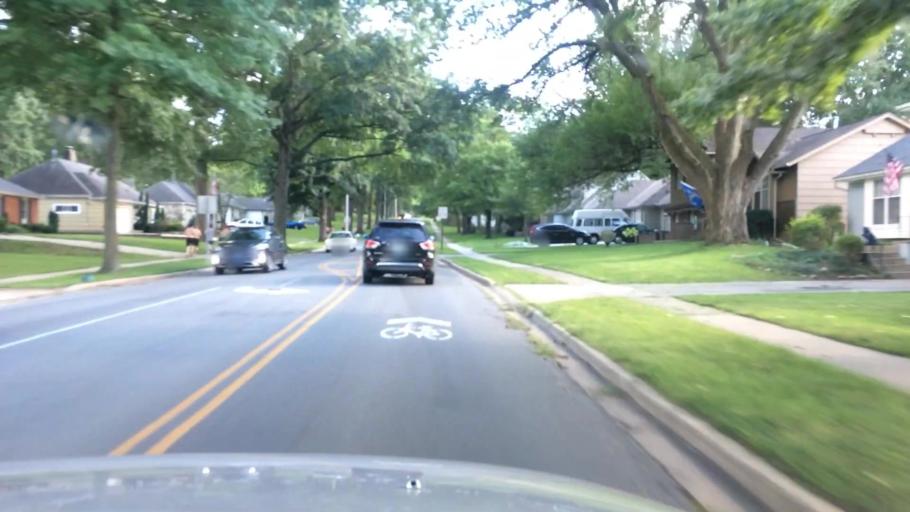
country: US
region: Kansas
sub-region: Johnson County
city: Overland Park
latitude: 38.9856
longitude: -94.6585
